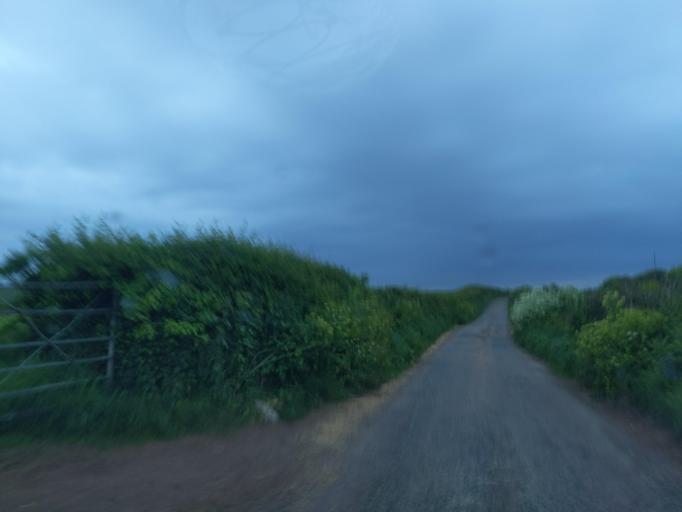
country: GB
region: England
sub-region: Devon
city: Dartmouth
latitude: 50.3575
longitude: -3.5378
